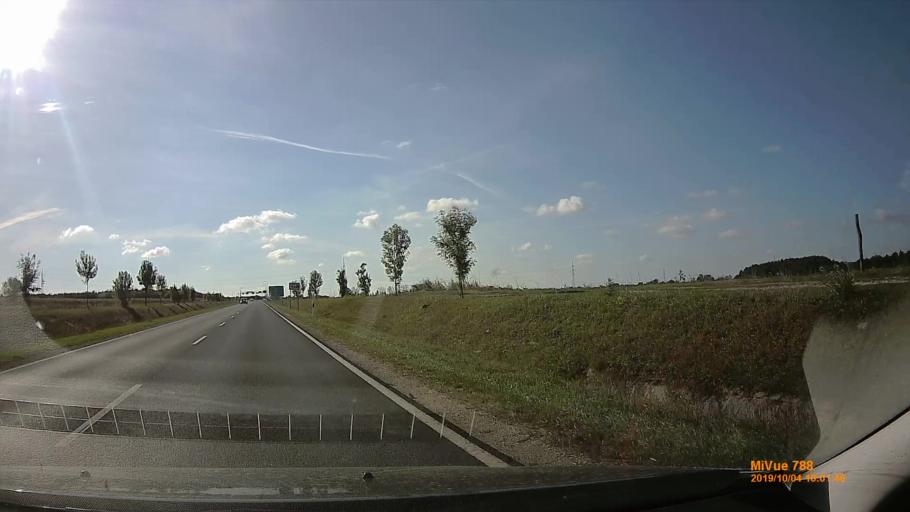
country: HU
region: Somogy
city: Kaposvar
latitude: 46.4027
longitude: 17.7740
